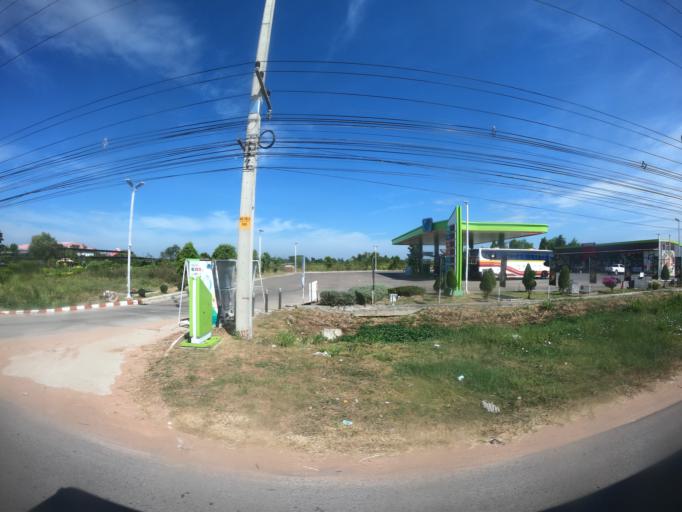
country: TH
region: Khon Kaen
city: Khon Kaen
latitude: 16.4378
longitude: 102.9273
